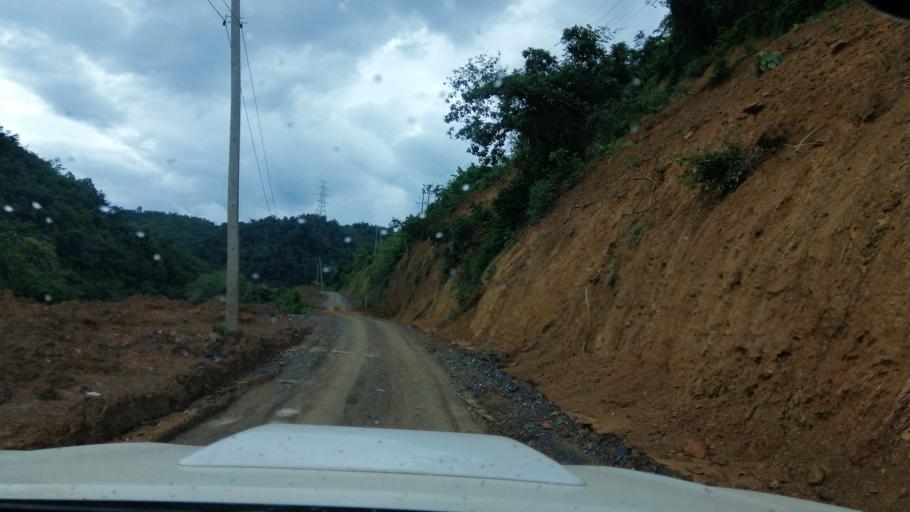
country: LA
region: Xiagnabouli
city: Sainyabuli
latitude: 19.1862
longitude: 101.7900
